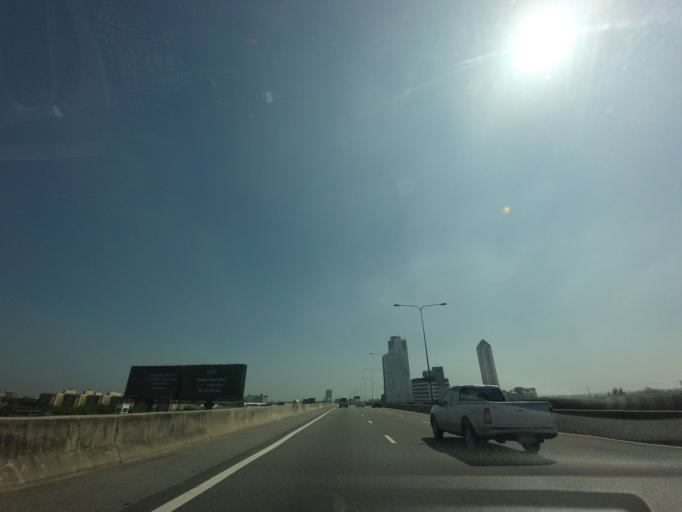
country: TH
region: Bangkok
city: Bang Na
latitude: 13.6657
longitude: 100.6454
